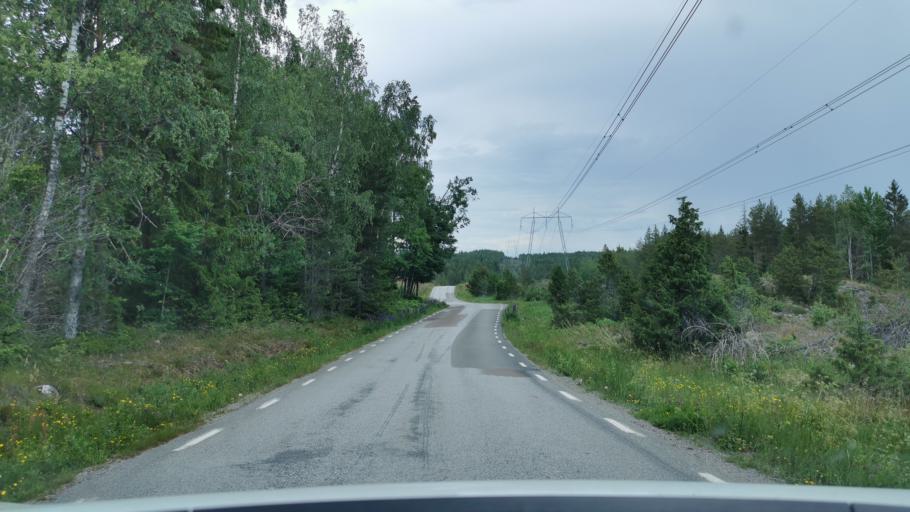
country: SE
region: Vaestra Goetaland
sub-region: Bengtsfors Kommun
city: Dals Langed
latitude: 58.8717
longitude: 12.4040
